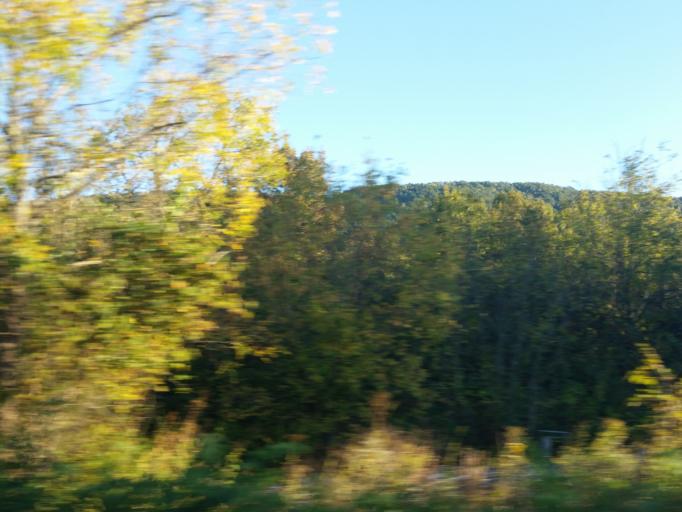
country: US
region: Tennessee
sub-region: Grainger County
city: Rutledge
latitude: 36.3381
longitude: -83.4871
